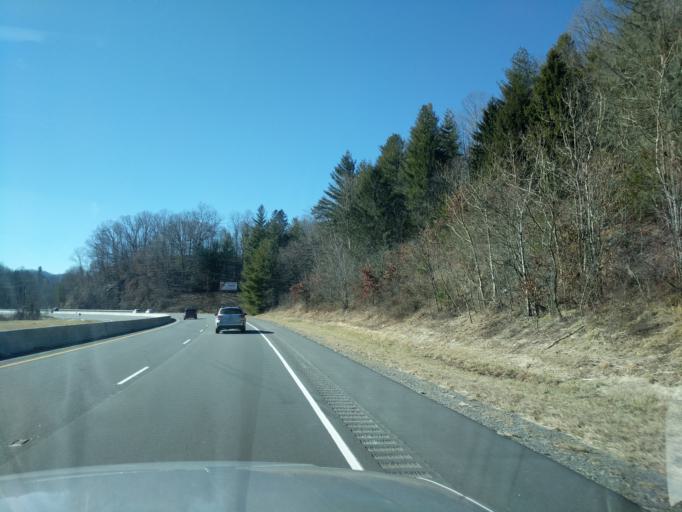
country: US
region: North Carolina
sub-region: Jackson County
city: Cullowhee
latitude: 35.4092
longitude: -83.1204
